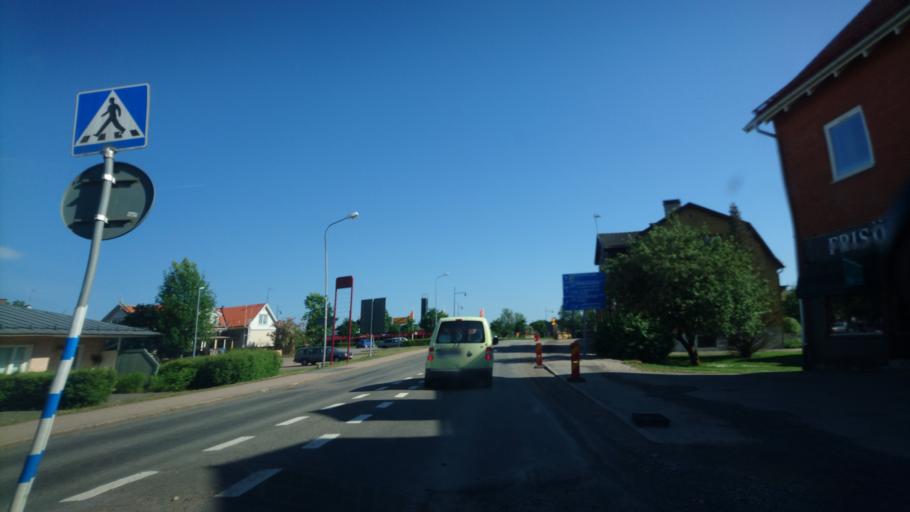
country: SE
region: Skane
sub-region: Osby Kommun
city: Lonsboda
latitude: 56.3985
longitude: 14.3196
